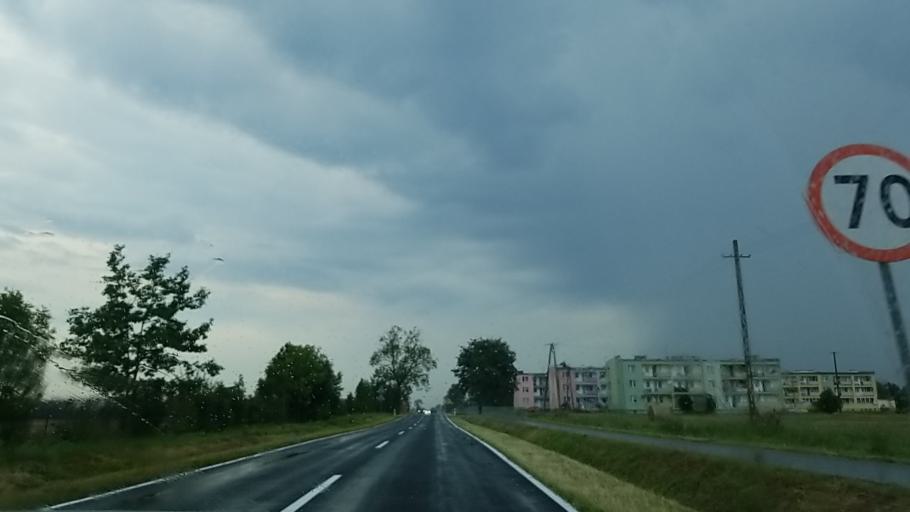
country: PL
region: Lublin Voivodeship
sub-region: Powiat wlodawski
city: Wlodawa
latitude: 51.6134
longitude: 23.5293
